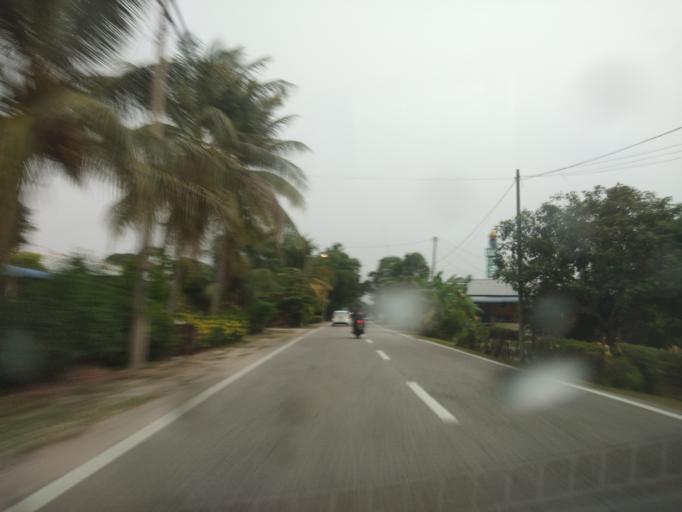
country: MY
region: Penang
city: Permatang Kuching
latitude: 5.4859
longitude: 100.4005
